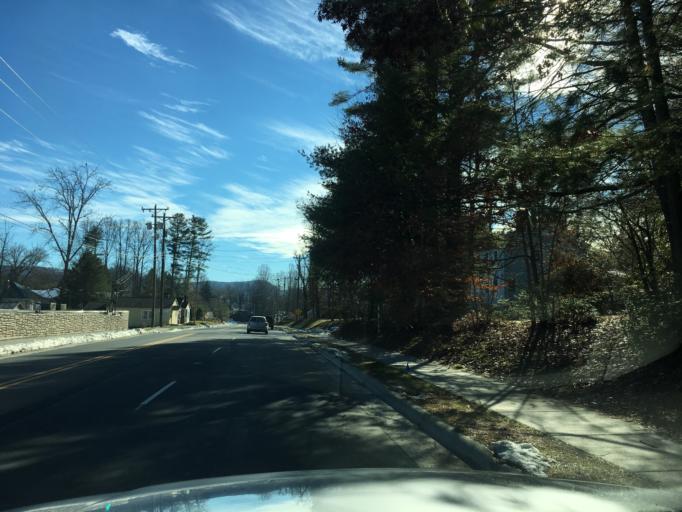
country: US
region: North Carolina
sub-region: Transylvania County
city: Brevard
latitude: 35.2293
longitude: -82.7387
